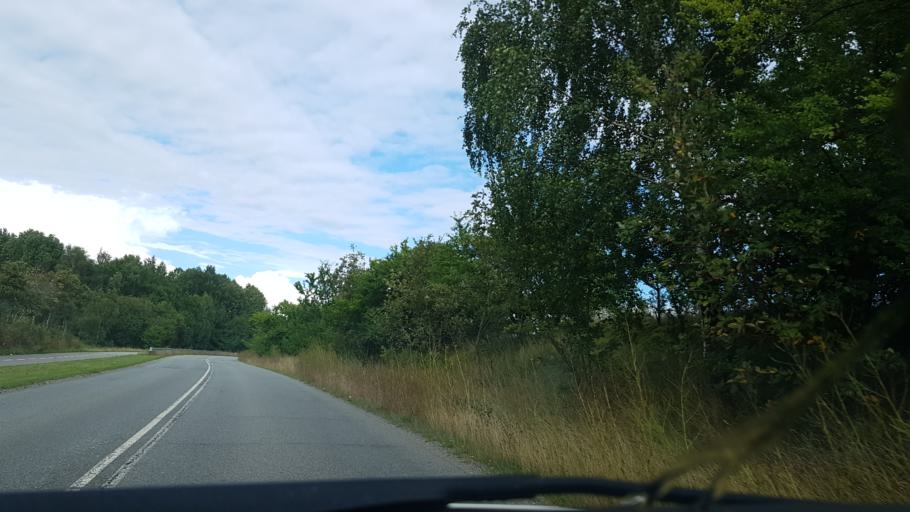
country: DK
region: Capital Region
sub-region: Fredensborg Kommune
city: Niva
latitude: 55.9667
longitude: 12.4832
